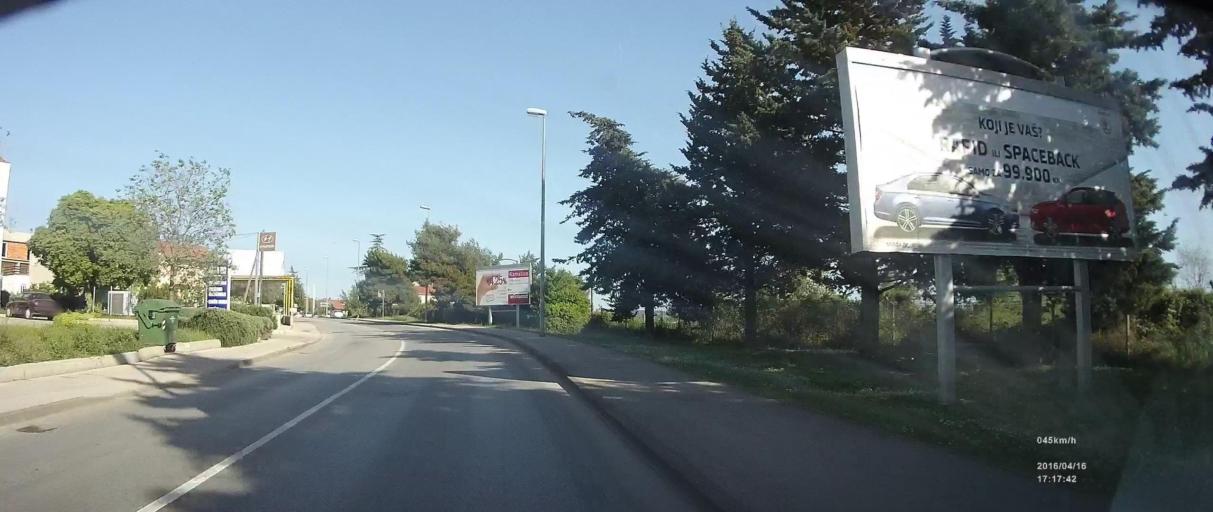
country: HR
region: Zadarska
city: Zadar
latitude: 44.1022
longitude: 15.2490
